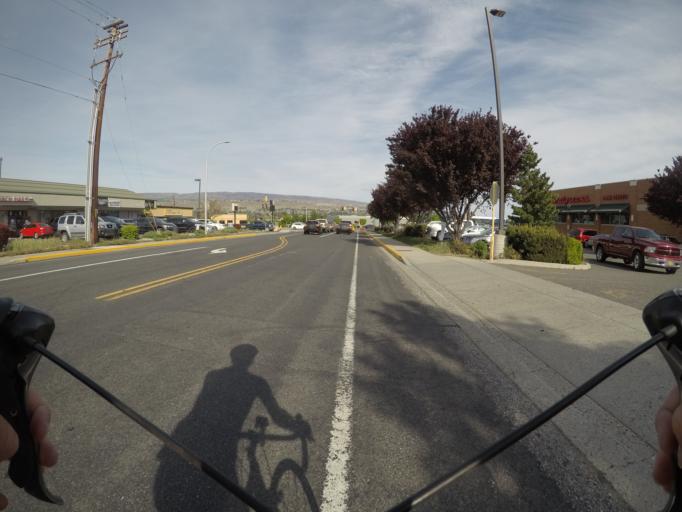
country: US
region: Washington
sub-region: Chelan County
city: Wenatchee
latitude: 47.4367
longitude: -120.3260
